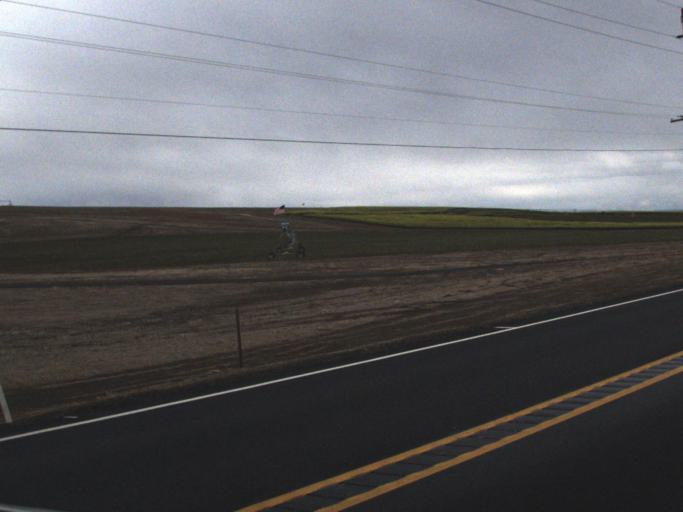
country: US
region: Washington
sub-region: Walla Walla County
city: Burbank
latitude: 46.0642
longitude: -118.7490
